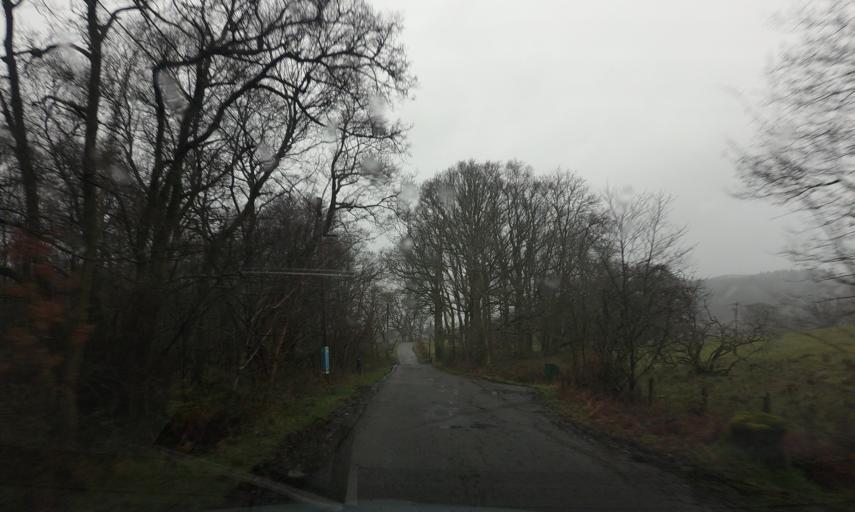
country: GB
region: Scotland
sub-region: West Dunbartonshire
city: Balloch
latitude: 56.1374
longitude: -4.6152
